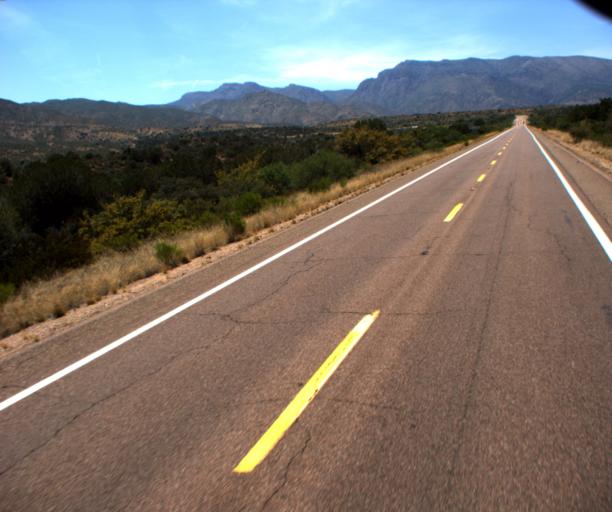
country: US
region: Arizona
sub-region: Gila County
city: Payson
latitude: 34.0310
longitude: -111.3545
